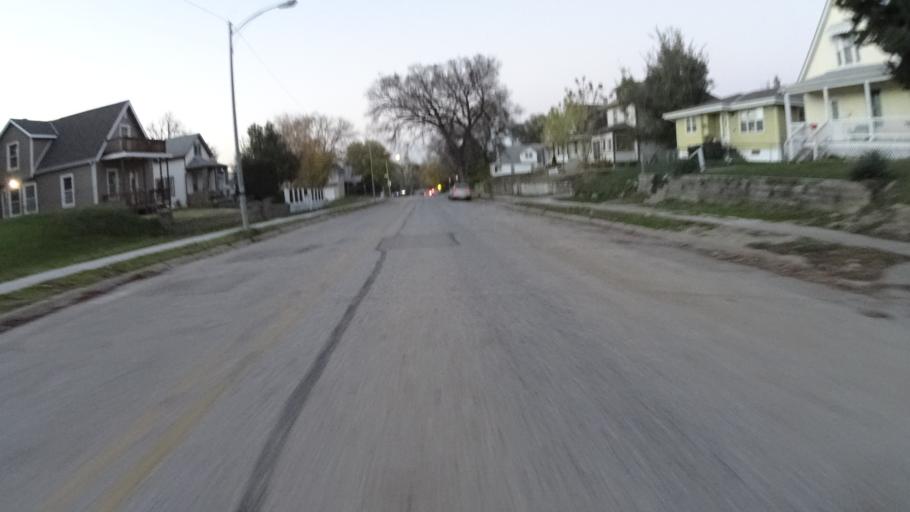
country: US
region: Nebraska
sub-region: Douglas County
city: Omaha
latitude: 41.2138
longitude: -95.9626
